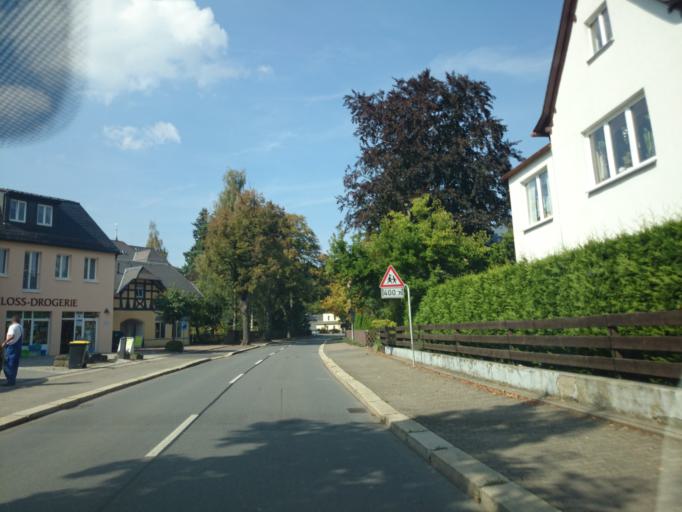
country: DE
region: Saxony
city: Augustusburg
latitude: 50.8080
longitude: 13.1017
